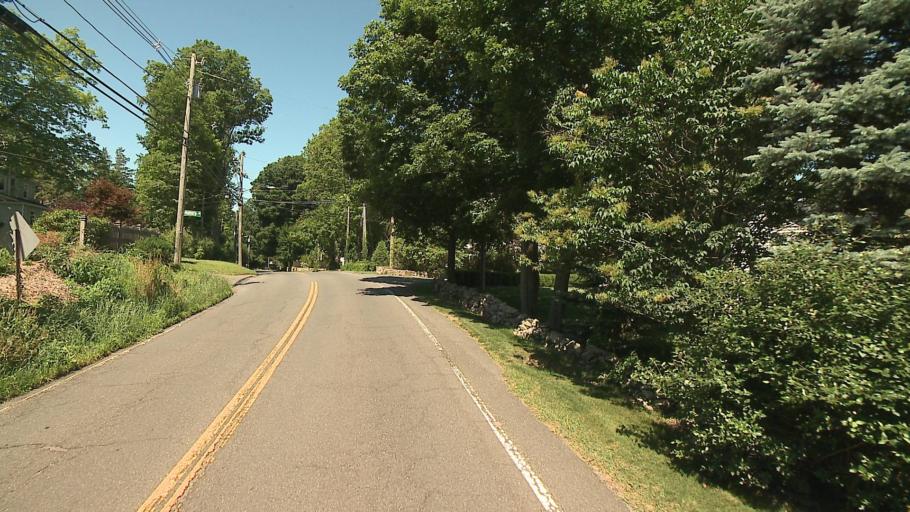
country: US
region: Connecticut
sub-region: Fairfield County
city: Ridgefield
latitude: 41.2824
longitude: -73.5079
